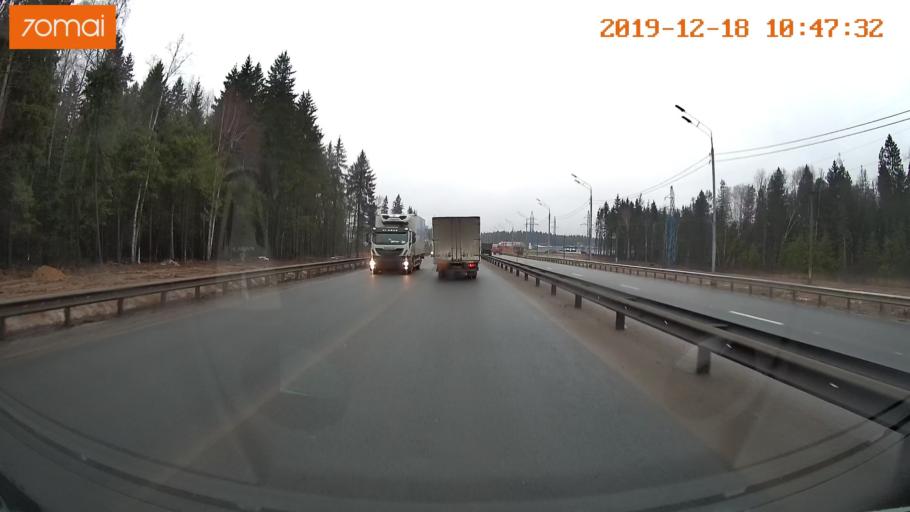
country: RU
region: Moskovskaya
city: Selyatino
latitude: 55.4914
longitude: 37.0363
